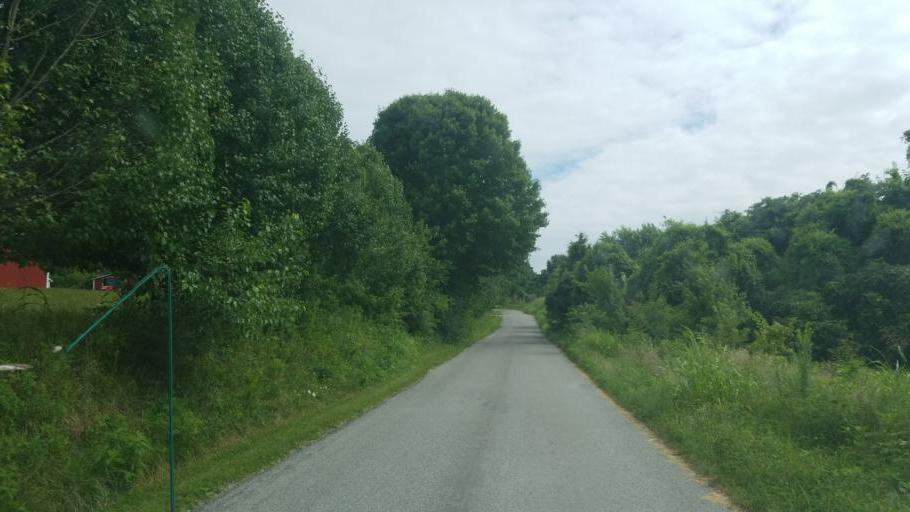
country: US
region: Illinois
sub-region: Union County
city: Cobden
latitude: 37.6167
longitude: -89.3711
